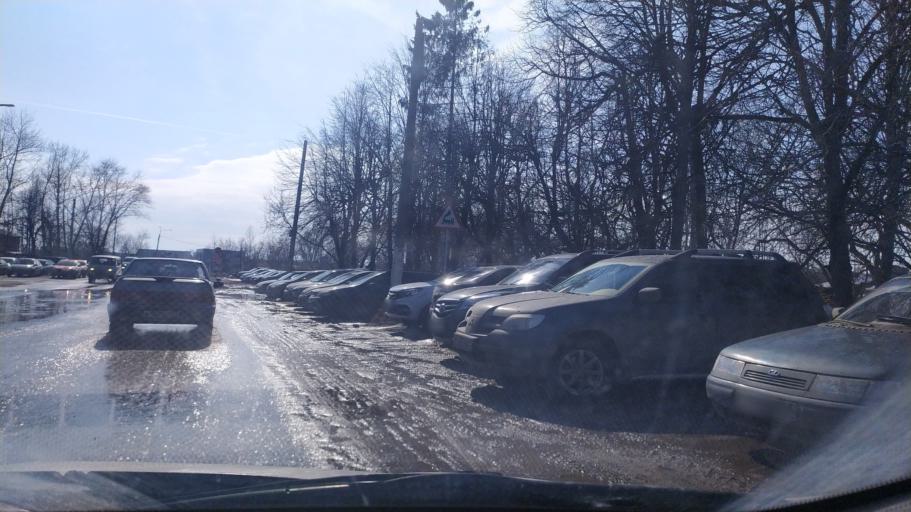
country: RU
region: Chuvashia
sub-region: Cheboksarskiy Rayon
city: Cheboksary
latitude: 56.1185
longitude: 47.2893
